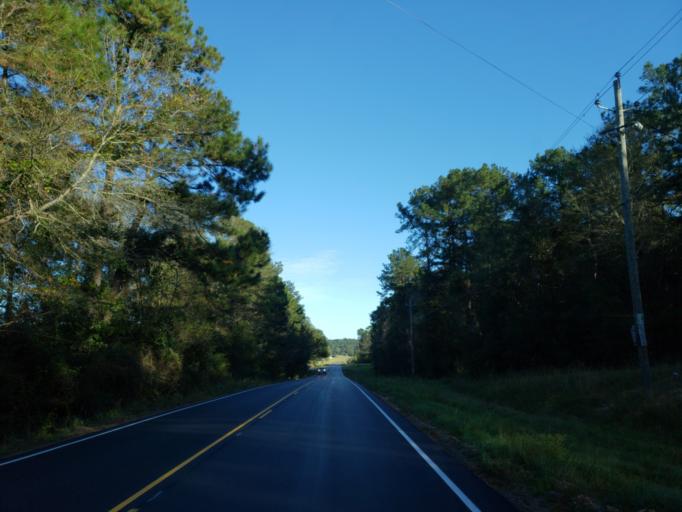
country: US
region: Mississippi
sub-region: Perry County
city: Richton
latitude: 31.3694
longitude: -88.8195
